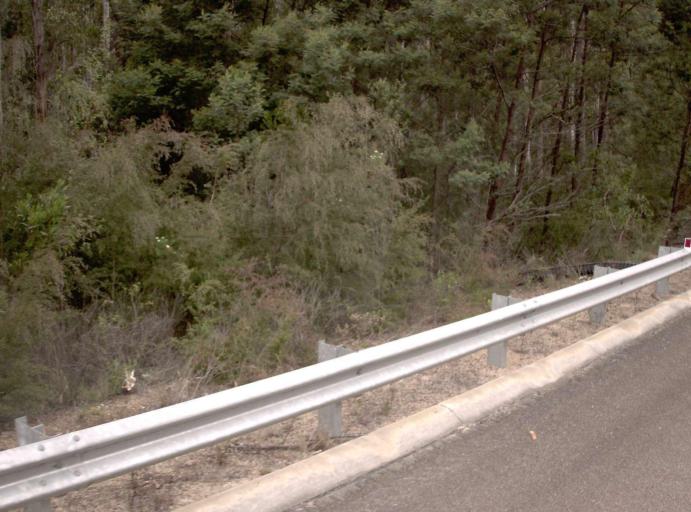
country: AU
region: Victoria
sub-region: East Gippsland
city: Lakes Entrance
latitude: -37.7193
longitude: 148.0787
